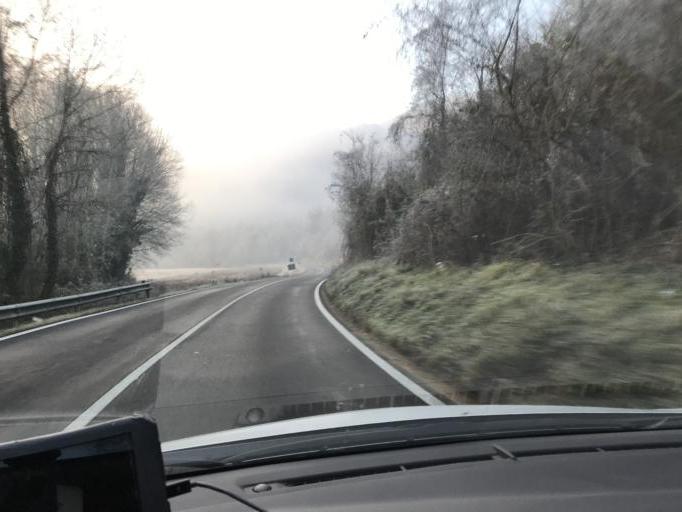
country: IT
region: Latium
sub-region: Provincia di Rieti
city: Colli sul Velino
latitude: 42.5224
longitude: 12.7344
